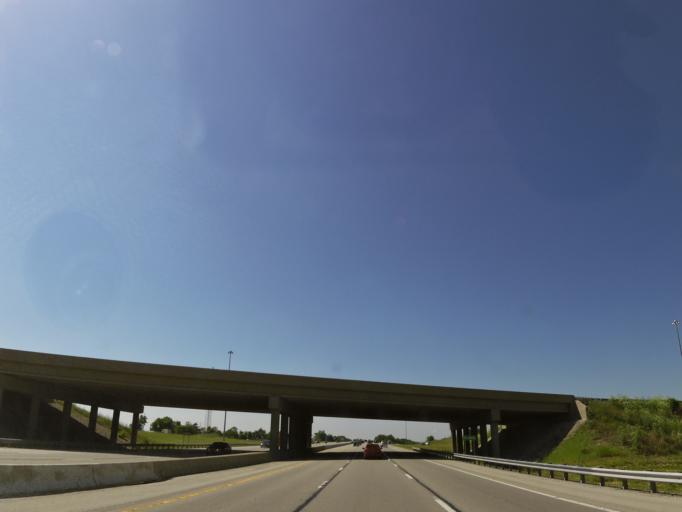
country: US
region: Kentucky
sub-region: Madison County
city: Richmond
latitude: 37.6751
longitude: -84.3119
